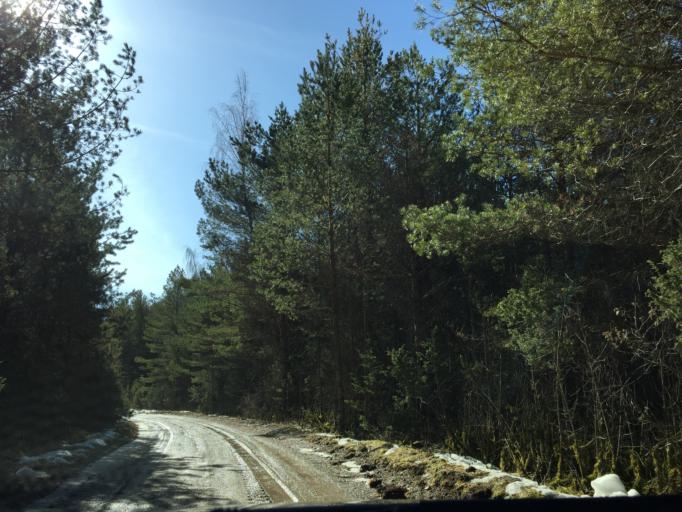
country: EE
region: Laeaene
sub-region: Haapsalu linn
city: Haapsalu
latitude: 58.6395
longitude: 23.5177
